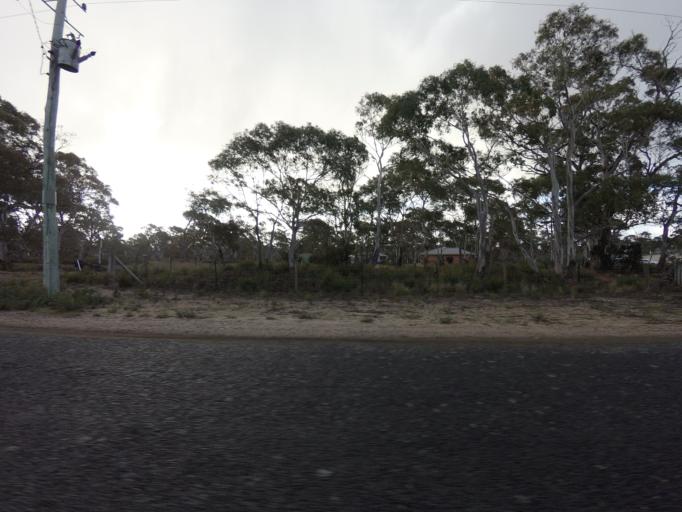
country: AU
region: Tasmania
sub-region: Break O'Day
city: St Helens
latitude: -42.1001
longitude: 148.0853
